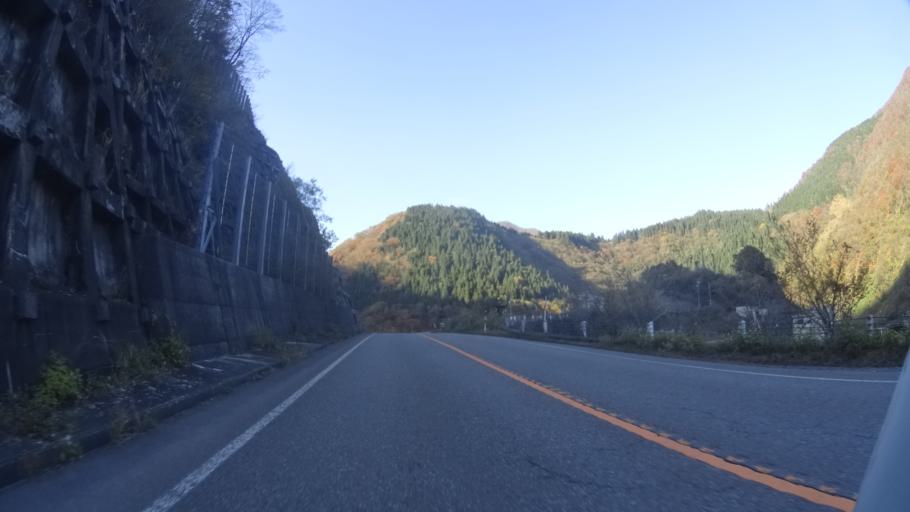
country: JP
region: Fukui
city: Ono
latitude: 35.9540
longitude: 136.6215
